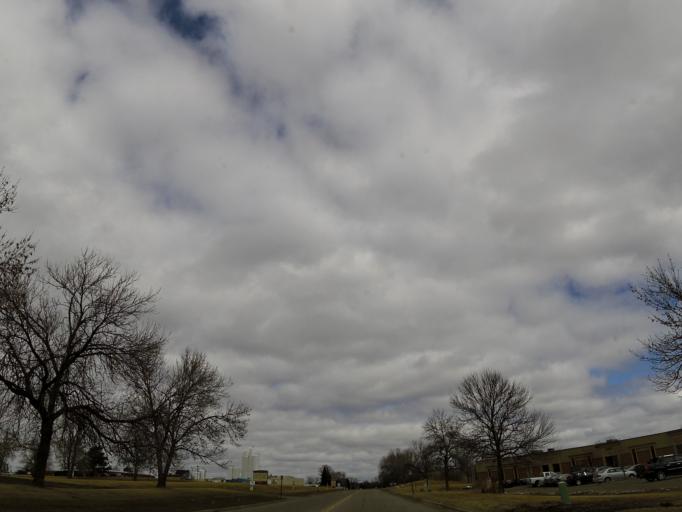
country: US
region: Minnesota
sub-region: Washington County
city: Woodbury
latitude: 44.9180
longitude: -92.9740
